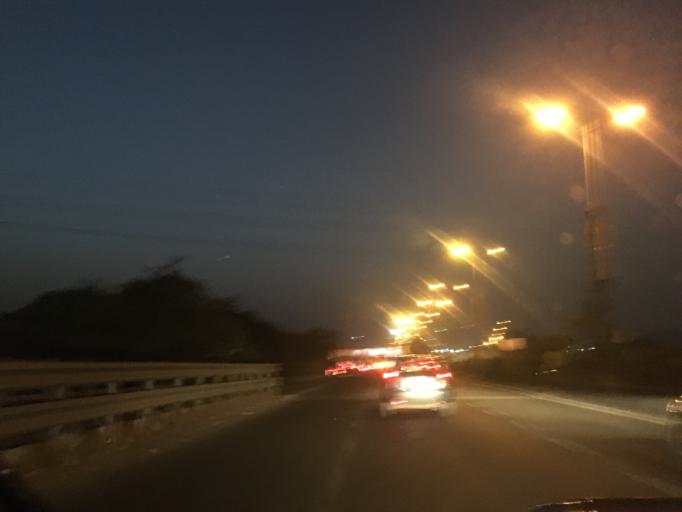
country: IN
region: Maharashtra
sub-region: Thane
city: Airoli
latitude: 19.1528
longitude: 72.9687
